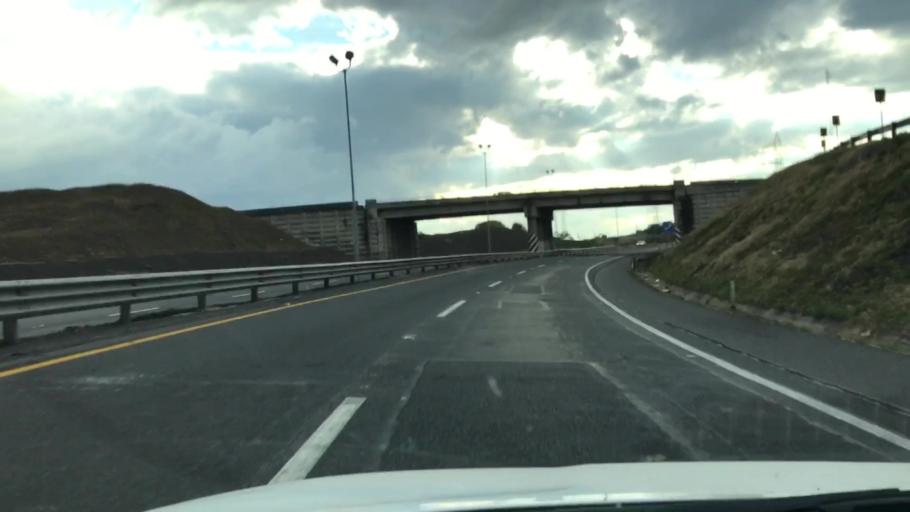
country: MX
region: Guanajuato
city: Penjamo
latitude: 20.4215
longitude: -101.7154
